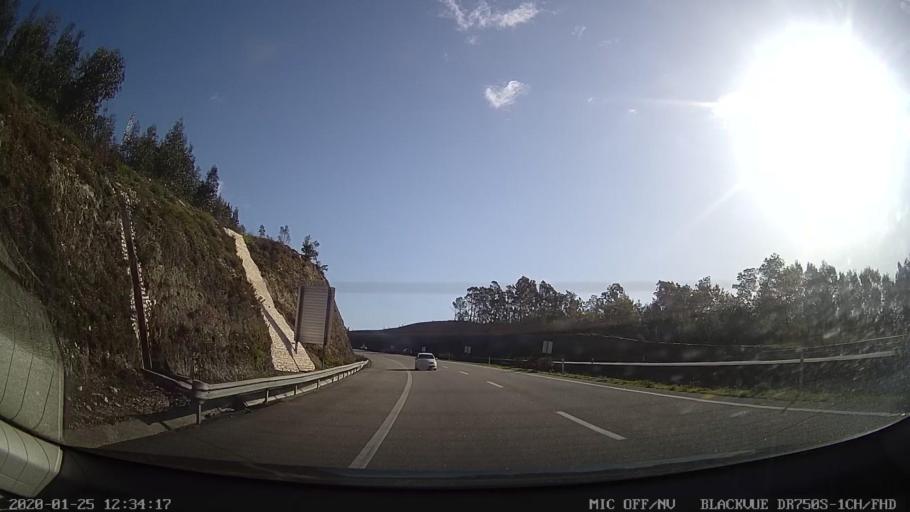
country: PT
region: Aveiro
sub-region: Agueda
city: Valongo
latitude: 40.6502
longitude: -8.3740
